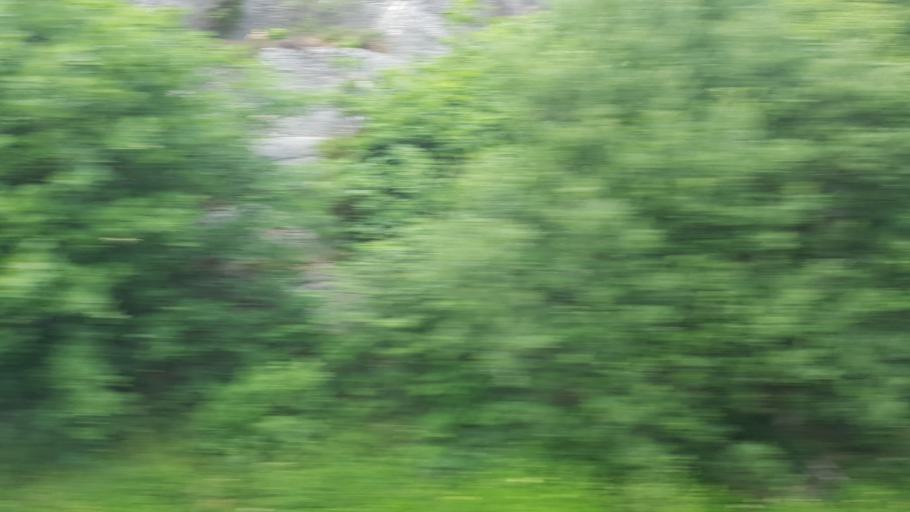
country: SE
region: Vaestra Goetaland
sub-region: Tjorns Kommun
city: Skaerhamn
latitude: 57.9640
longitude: 11.5621
